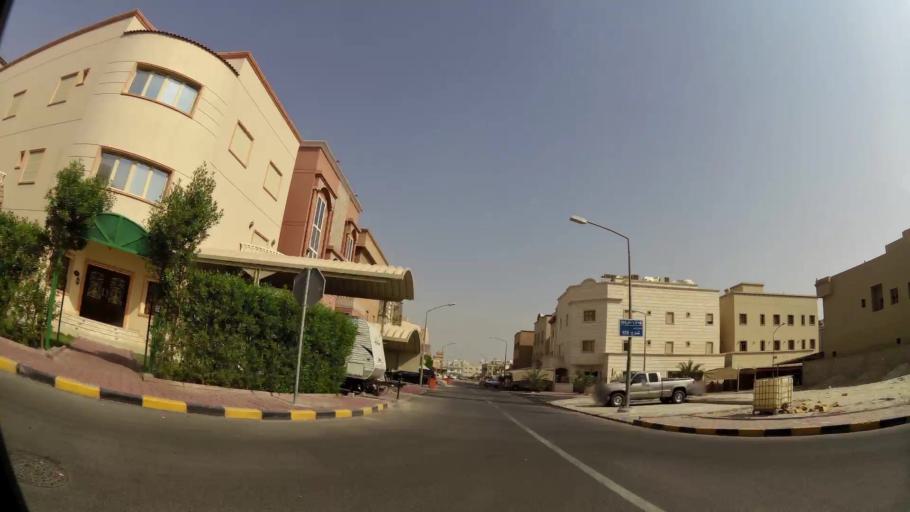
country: KW
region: Muhafazat al Jahra'
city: Al Jahra'
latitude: 29.3268
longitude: 47.7749
